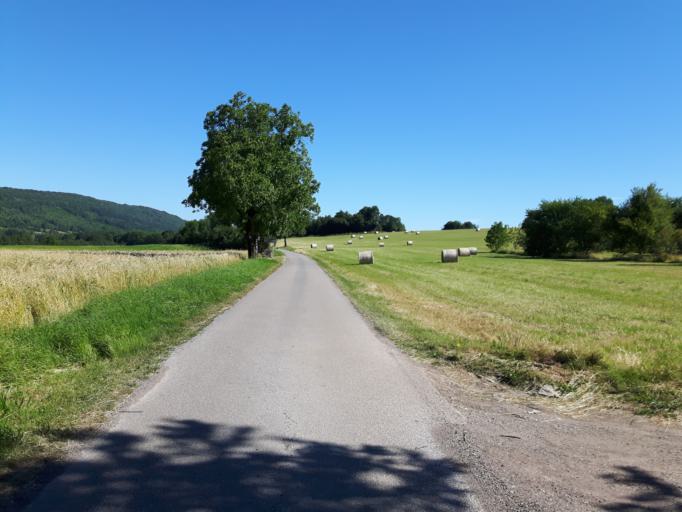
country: FR
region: Franche-Comte
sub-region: Departement du Jura
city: Salins-les-Bains
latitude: 47.0011
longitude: 5.8562
